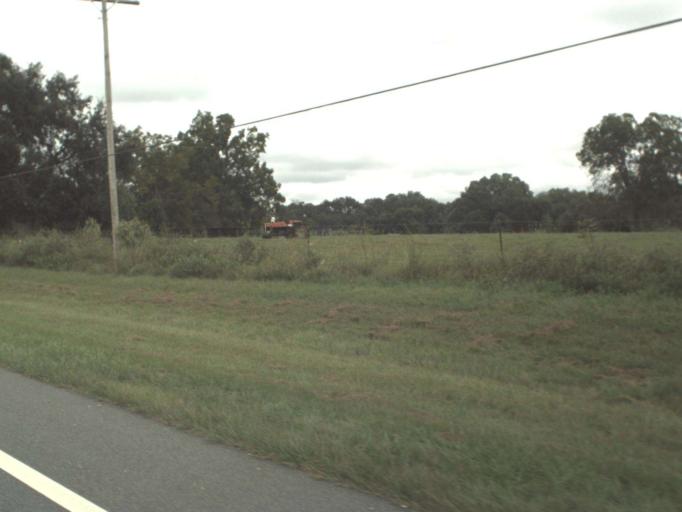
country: US
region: Florida
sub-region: Jackson County
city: Malone
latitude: 30.8480
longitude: -85.0721
